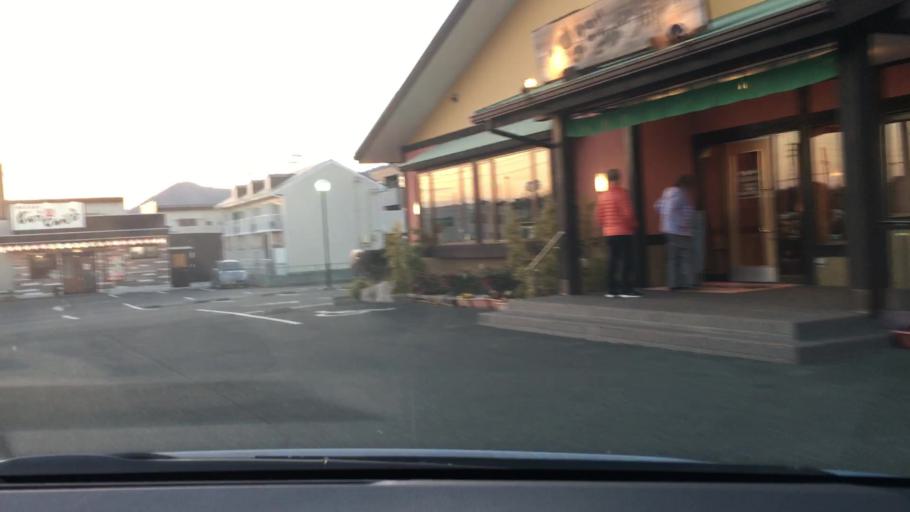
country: JP
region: Aichi
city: Tahara
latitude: 34.6611
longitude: 137.2681
